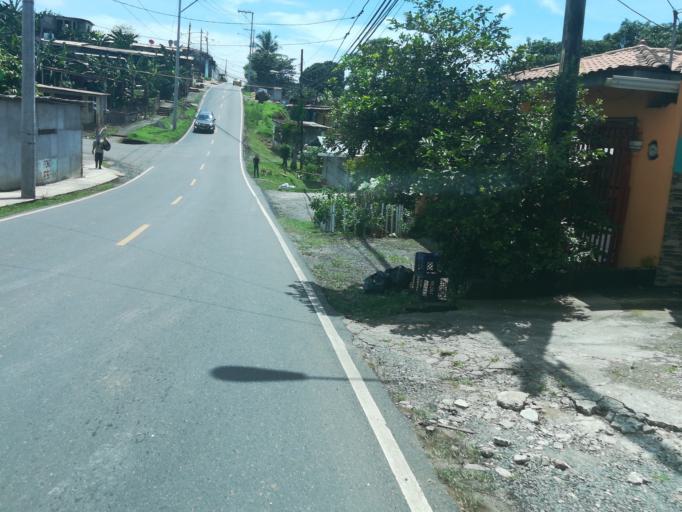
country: PA
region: Panama
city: Tocumen
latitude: 9.0941
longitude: -79.4048
